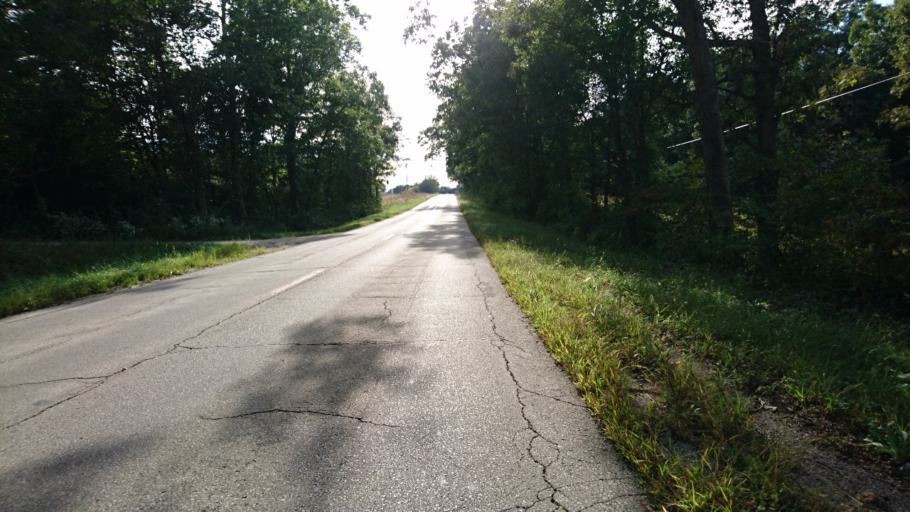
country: US
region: Missouri
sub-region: Crawford County
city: Cuba
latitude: 38.0971
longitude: -91.3586
